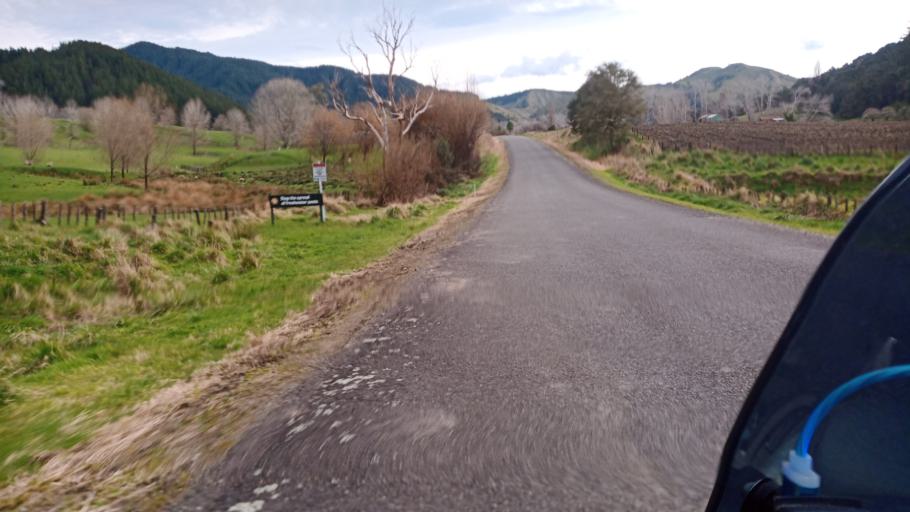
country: NZ
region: Hawke's Bay
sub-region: Wairoa District
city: Wairoa
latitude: -38.8205
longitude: 177.4914
